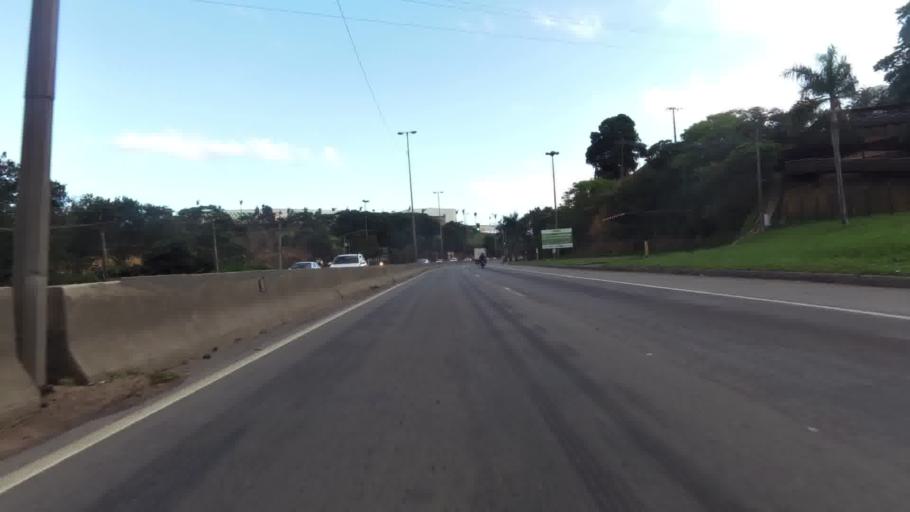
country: BR
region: Espirito Santo
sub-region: Vitoria
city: Vitoria
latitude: -20.3499
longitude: -40.4126
